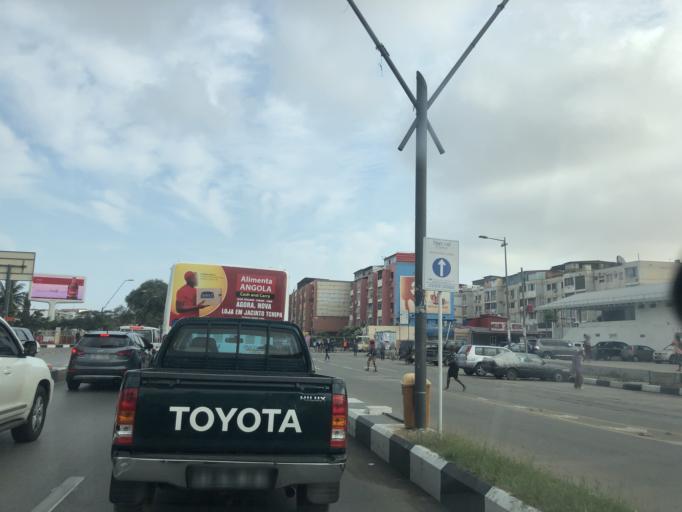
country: AO
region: Luanda
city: Luanda
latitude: -8.8451
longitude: 13.2338
